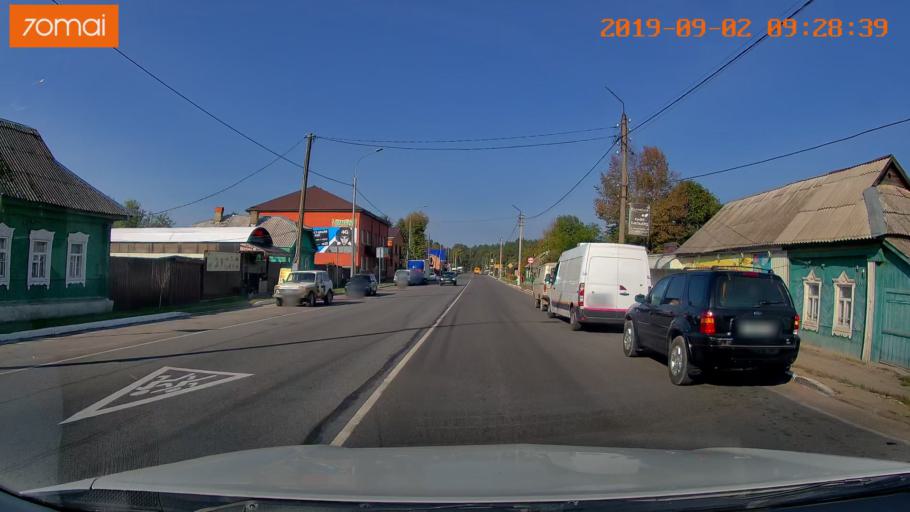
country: RU
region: Kaluga
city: Yukhnov
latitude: 54.7440
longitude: 35.2260
